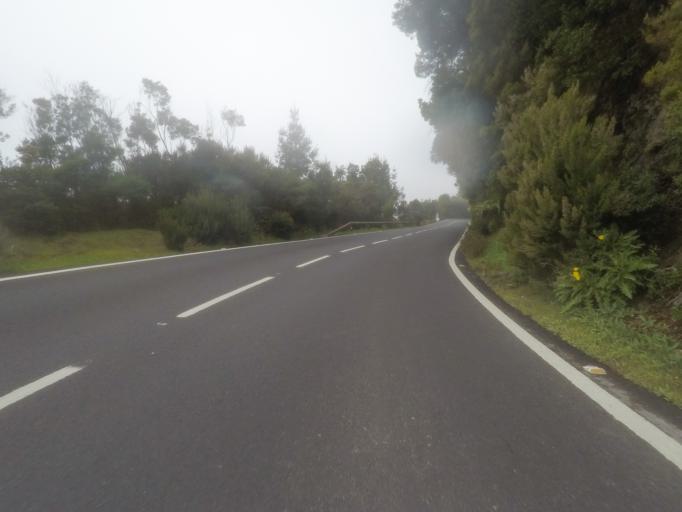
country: ES
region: Canary Islands
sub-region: Provincia de Santa Cruz de Tenerife
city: Alajero
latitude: 28.1168
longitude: -17.2460
